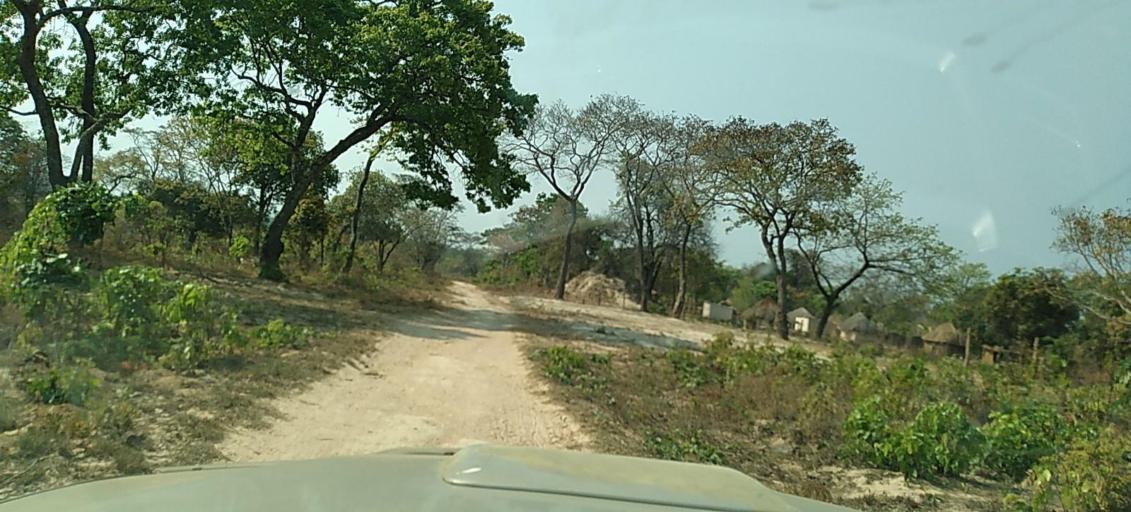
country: ZM
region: North-Western
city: Kasempa
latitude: -13.5430
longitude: 26.4088
